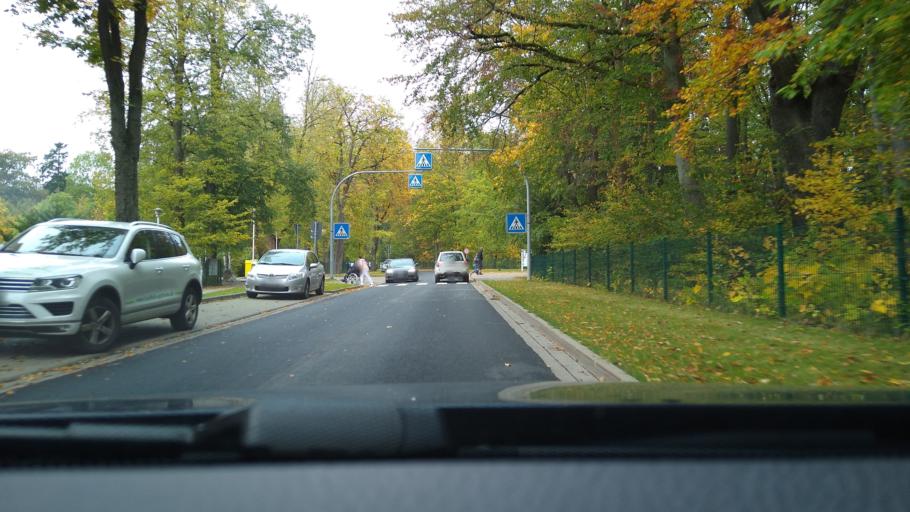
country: DE
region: Saxony-Anhalt
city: Elbingerode
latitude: 51.7728
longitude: 10.7913
